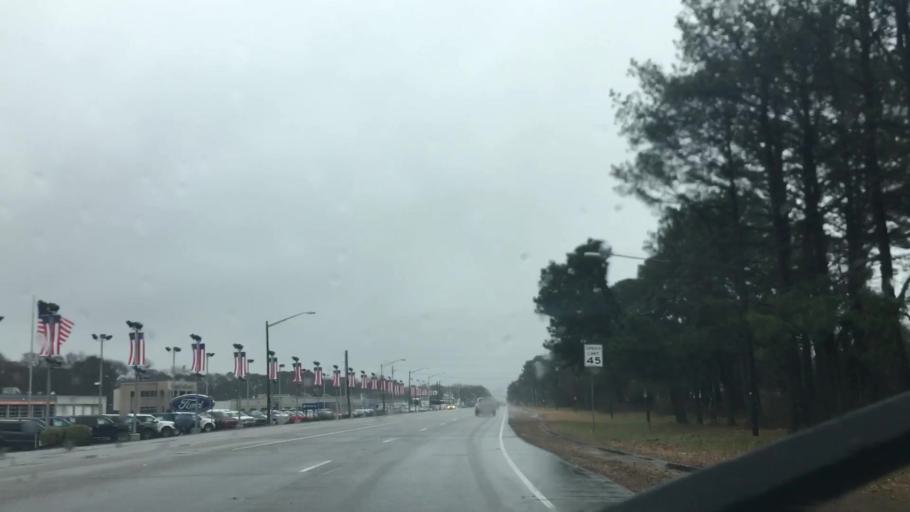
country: US
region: Virginia
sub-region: City of Norfolk
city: Norfolk
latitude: 36.9134
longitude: -76.2373
